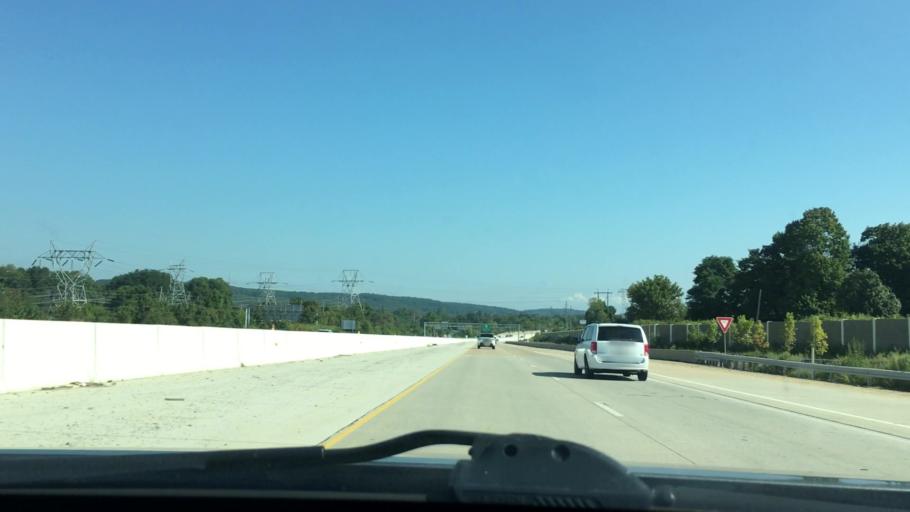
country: US
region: Pennsylvania
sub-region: Chester County
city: Exton
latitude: 40.0340
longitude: -75.5842
